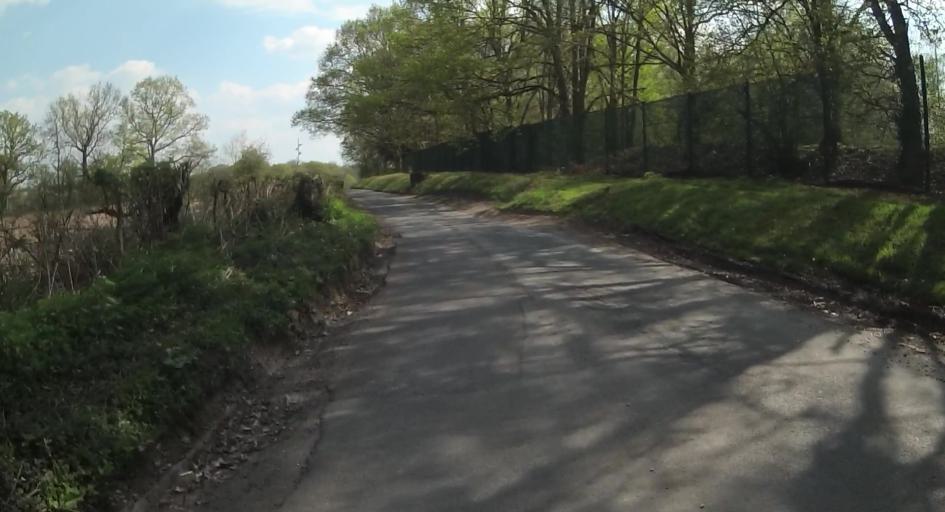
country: GB
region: England
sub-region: Hampshire
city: Tadley
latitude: 51.3891
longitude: -1.1059
